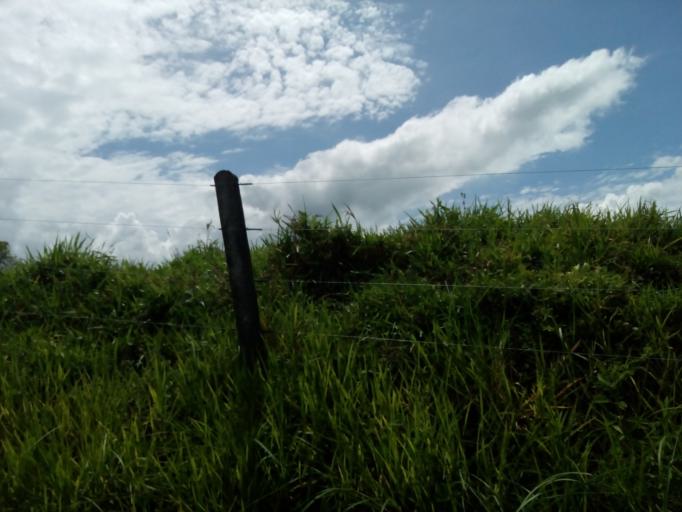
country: CO
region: Boyaca
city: Puerto Boyaca
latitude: 5.9905
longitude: -74.4084
